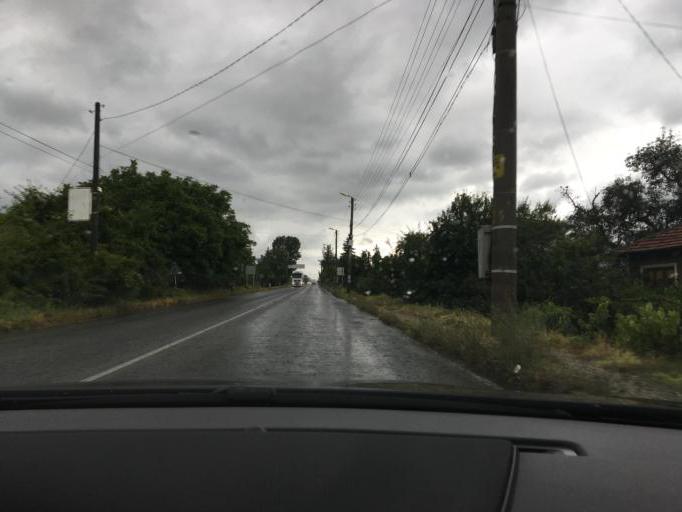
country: BG
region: Kyustendil
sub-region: Obshtina Kyustendil
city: Kyustendil
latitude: 42.2726
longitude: 22.6518
